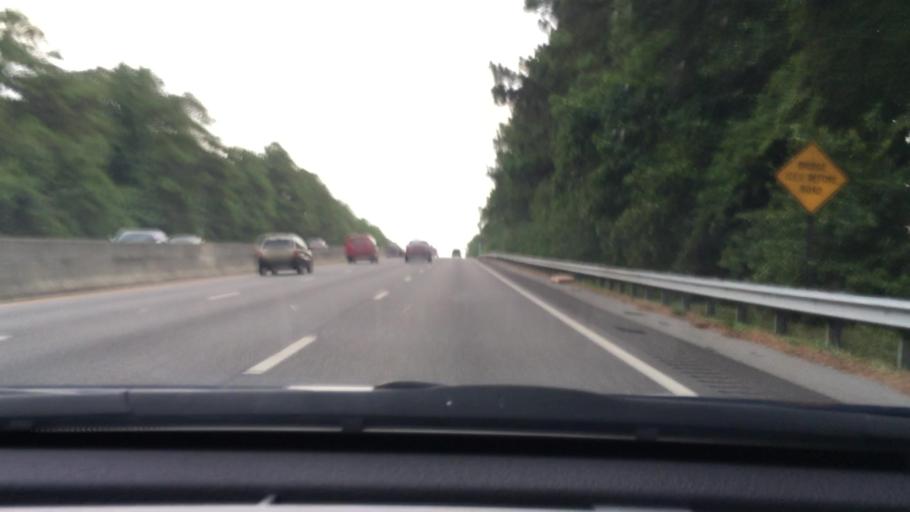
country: US
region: South Carolina
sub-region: Lexington County
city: Springdale
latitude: 33.9489
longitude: -81.0910
